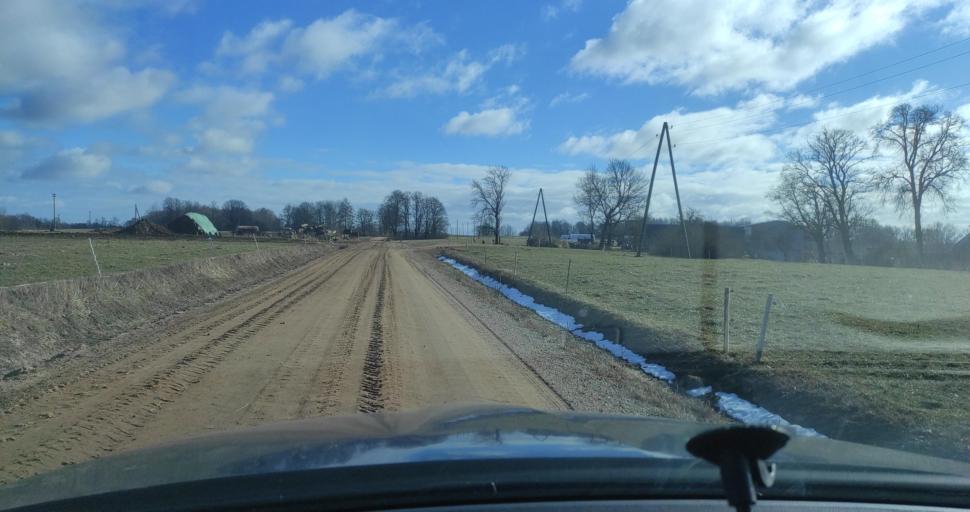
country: LV
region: Vainode
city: Vainode
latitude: 56.5144
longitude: 21.8593
